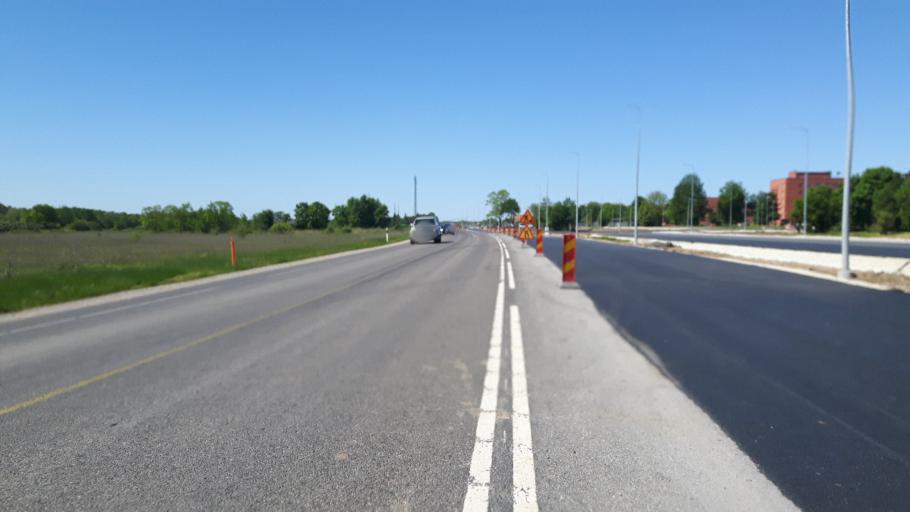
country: EE
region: Ida-Virumaa
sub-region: Sillamaee linn
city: Sillamae
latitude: 59.3888
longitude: 27.7990
